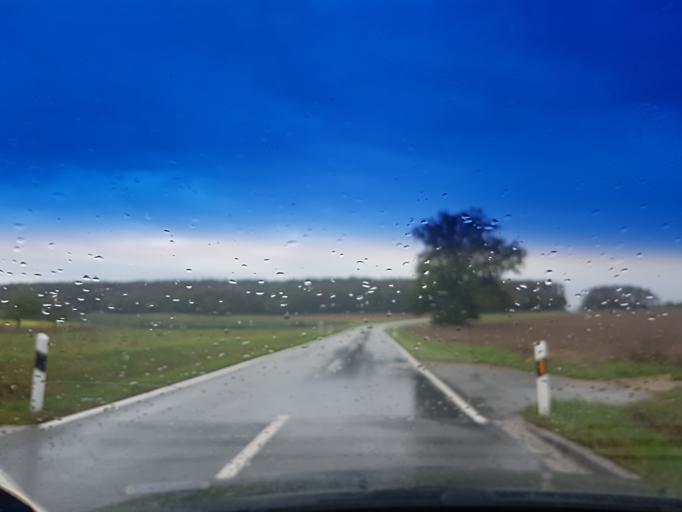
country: DE
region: Bavaria
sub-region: Regierungsbezirk Mittelfranken
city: Wachenroth
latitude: 49.7535
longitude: 10.6663
